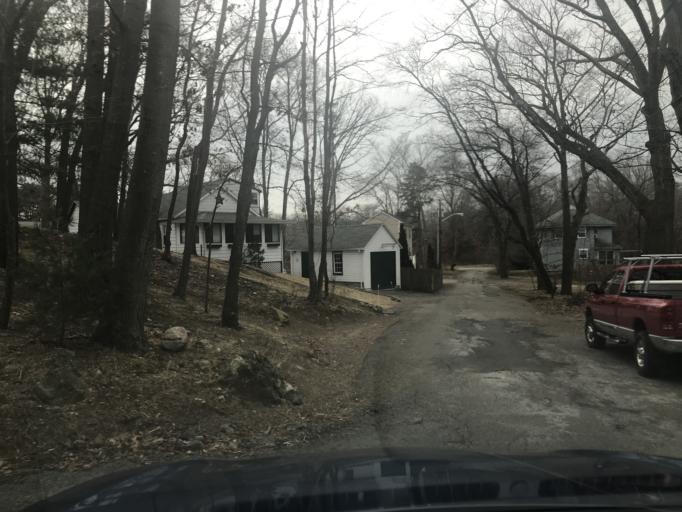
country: US
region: Massachusetts
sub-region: Essex County
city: Saugus
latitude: 42.4959
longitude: -71.0127
